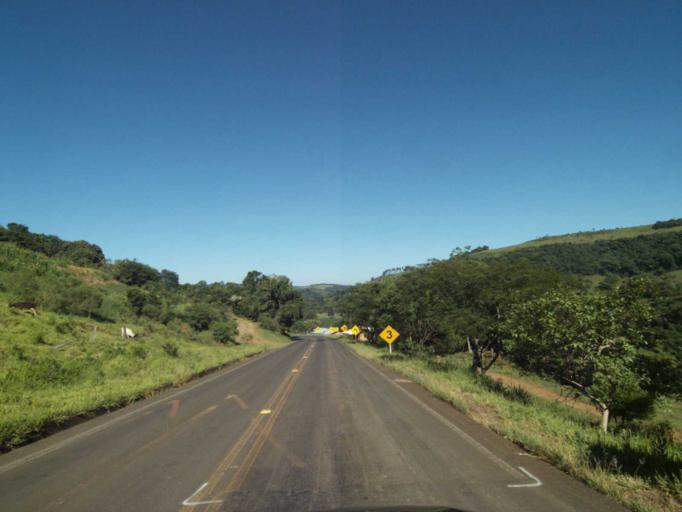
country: BR
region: Parana
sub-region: Francisco Beltrao
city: Francisco Beltrao
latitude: -26.1431
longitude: -53.3015
